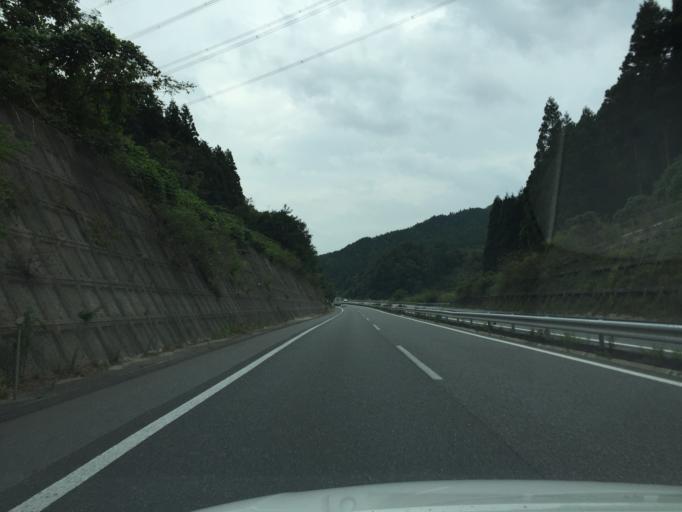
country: JP
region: Fukushima
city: Iwaki
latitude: 37.1487
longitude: 140.7416
